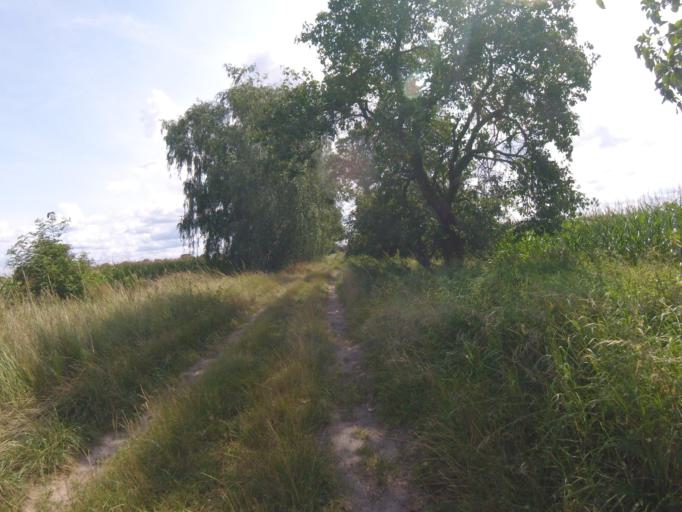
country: DE
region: Brandenburg
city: Mittenwalde
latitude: 52.2860
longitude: 13.5065
